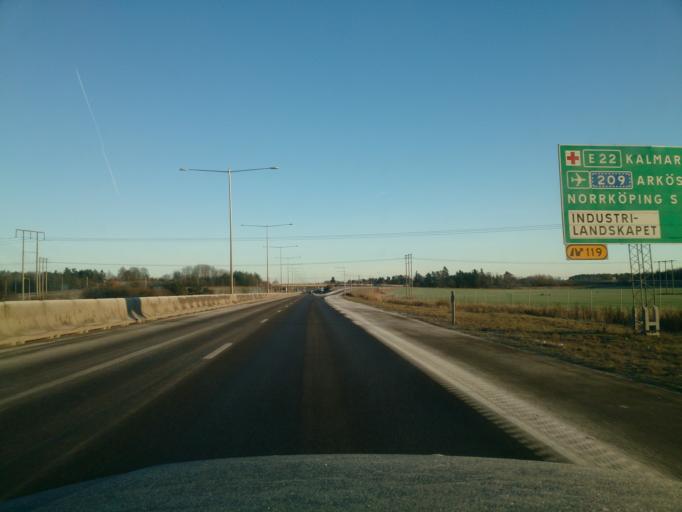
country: SE
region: OEstergoetland
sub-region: Norrkopings Kommun
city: Norrkoping
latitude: 58.5775
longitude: 16.1042
